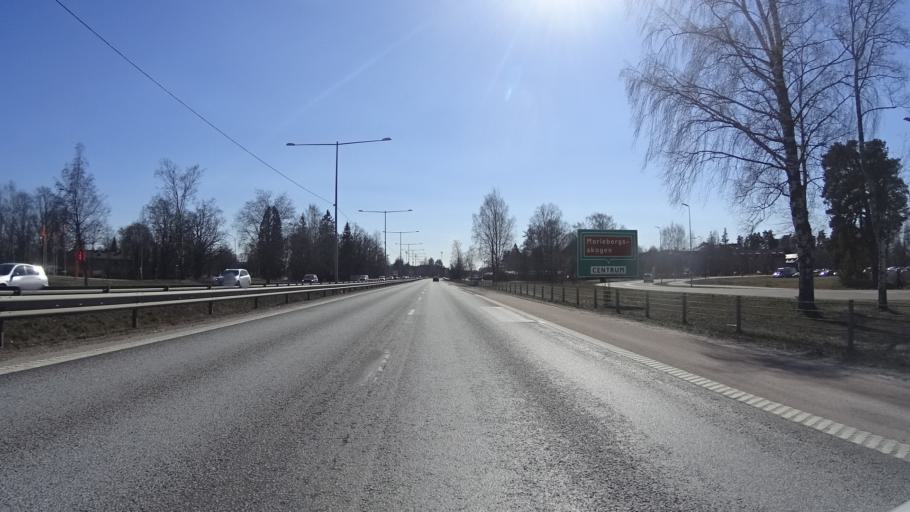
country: SE
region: Vaermland
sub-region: Karlstads Kommun
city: Karlstad
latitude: 59.3918
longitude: 13.4951
